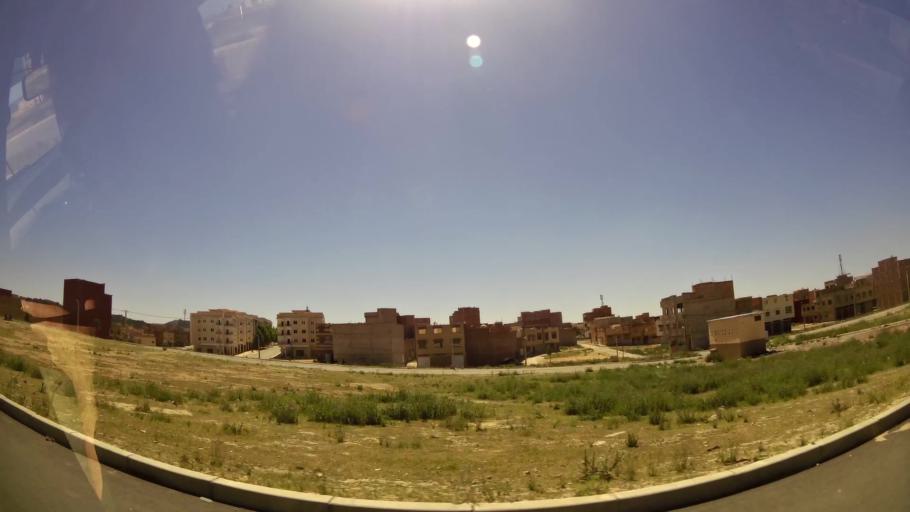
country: MA
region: Oriental
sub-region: Oujda-Angad
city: Oujda
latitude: 34.6572
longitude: -1.8720
